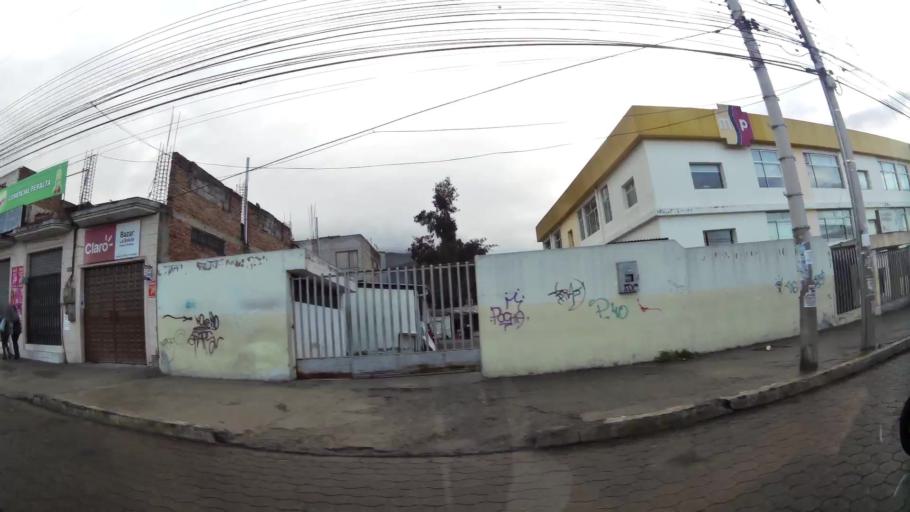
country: EC
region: Pichincha
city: Quito
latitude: -0.1127
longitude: -78.4912
